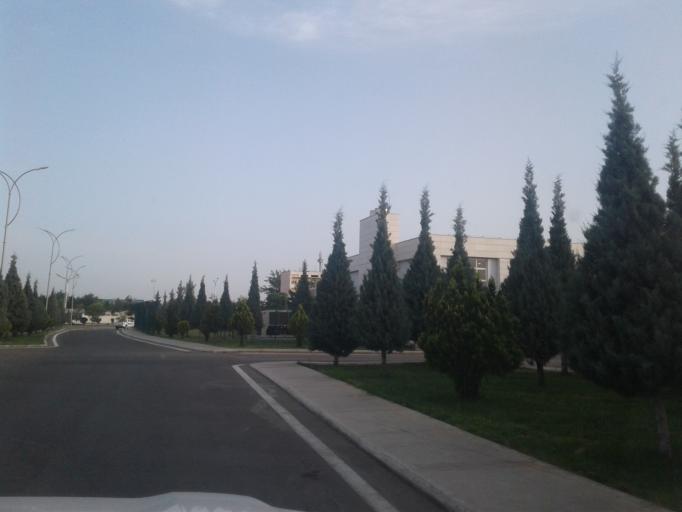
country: TM
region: Balkan
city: Turkmenbasy
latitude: 40.0425
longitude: 52.9935
